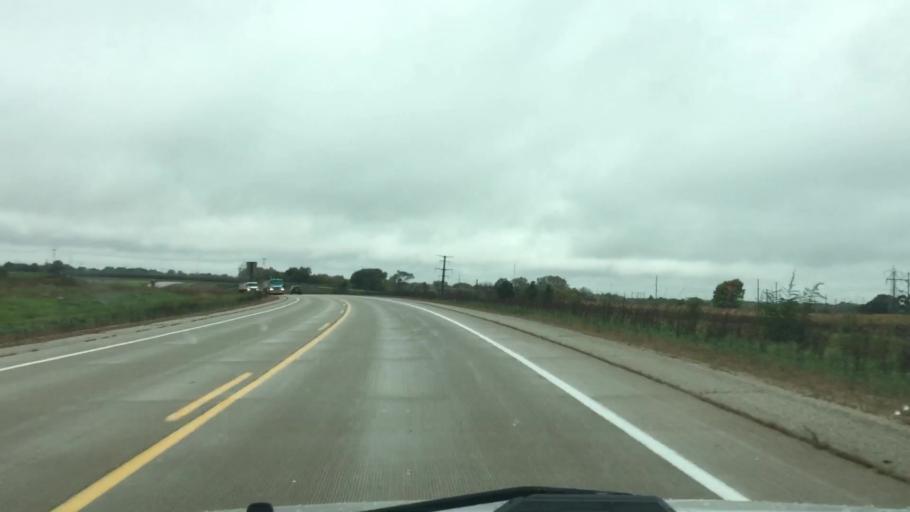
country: US
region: Wisconsin
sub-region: Walworth County
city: Whitewater
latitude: 42.8191
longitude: -88.7233
